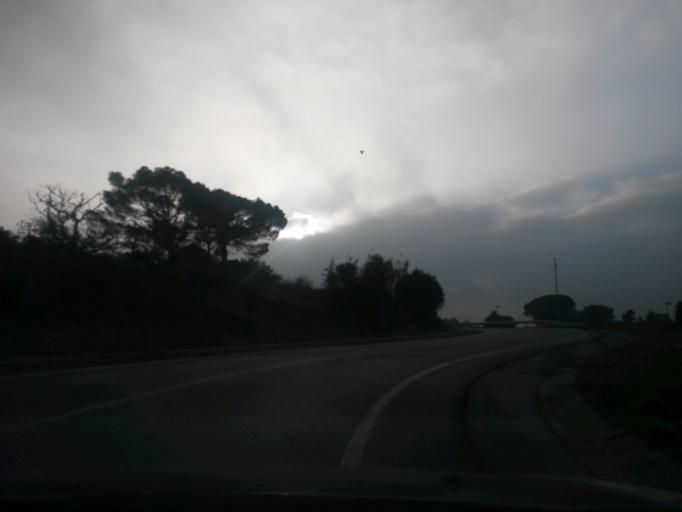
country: ES
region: Catalonia
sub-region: Provincia de Girona
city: Llagostera
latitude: 41.8307
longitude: 2.9090
